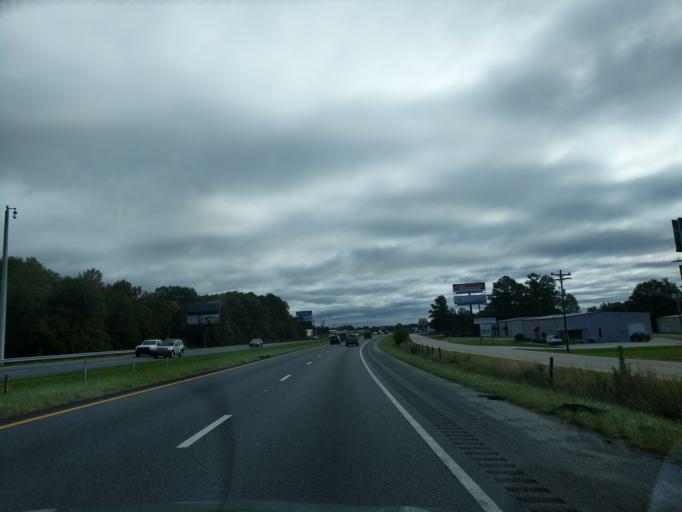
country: US
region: South Carolina
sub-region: Cherokee County
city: East Gaffney
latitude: 35.1018
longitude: -81.6424
